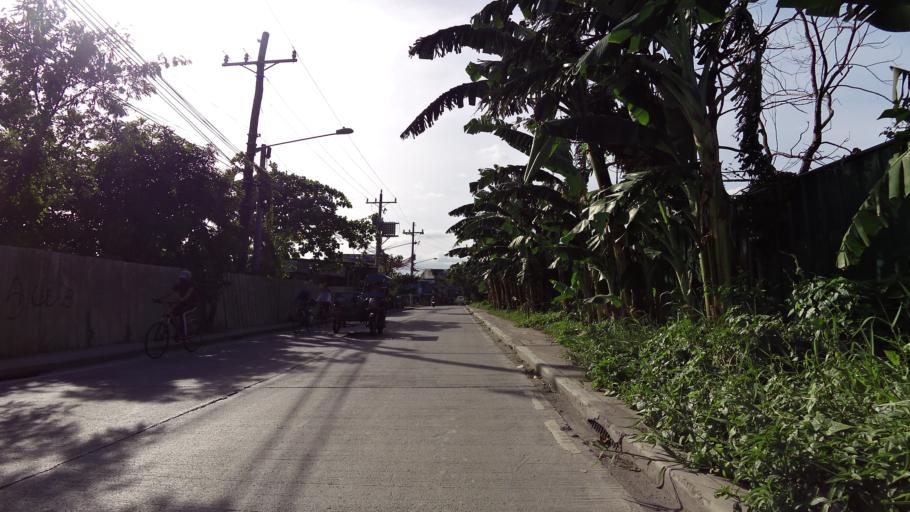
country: PH
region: Calabarzon
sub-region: Province of Rizal
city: Taytay
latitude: 14.5422
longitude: 121.1110
